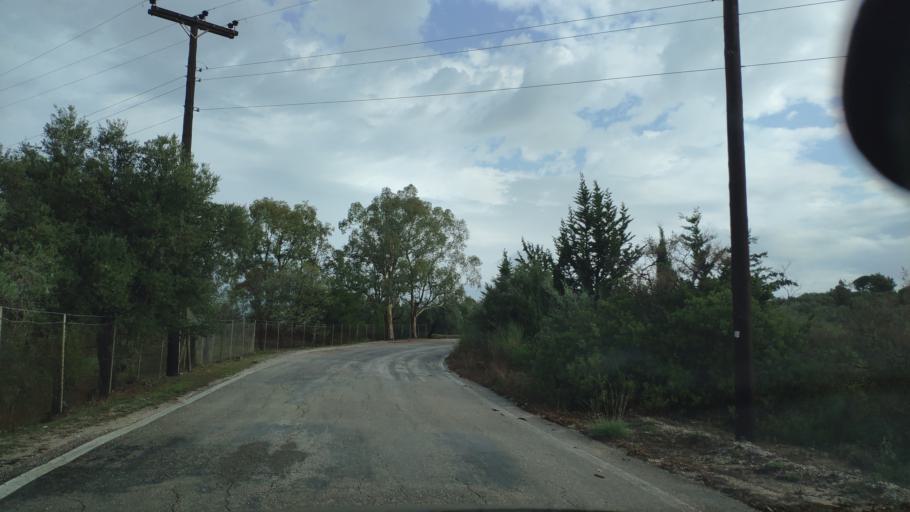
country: GR
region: West Greece
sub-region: Nomos Aitolias kai Akarnanias
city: Sardinia
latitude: 38.8886
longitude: 21.2180
